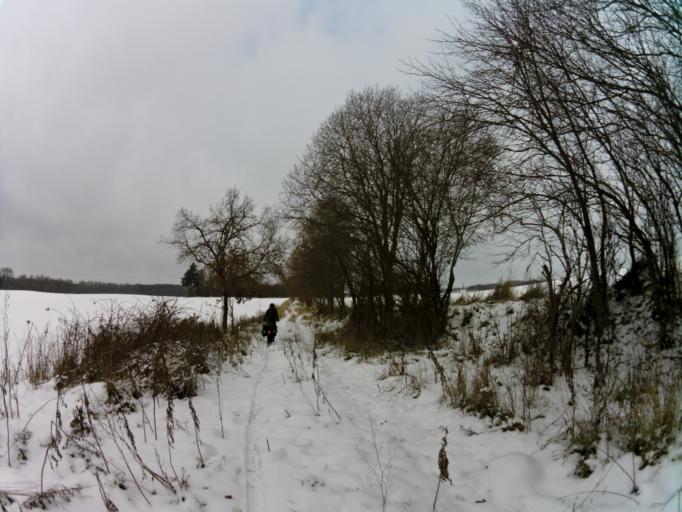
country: PL
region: West Pomeranian Voivodeship
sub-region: Powiat choszczenski
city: Recz
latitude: 53.3085
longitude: 15.5564
